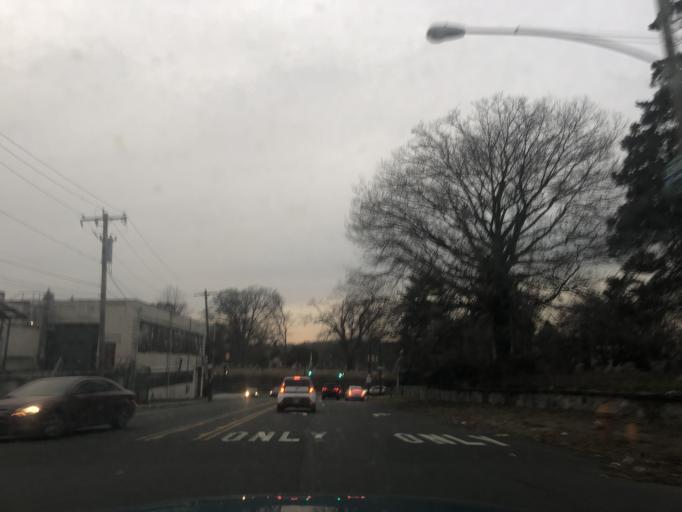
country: US
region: Pennsylvania
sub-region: Montgomery County
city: Bala-Cynwyd
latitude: 39.9981
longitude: -75.1864
